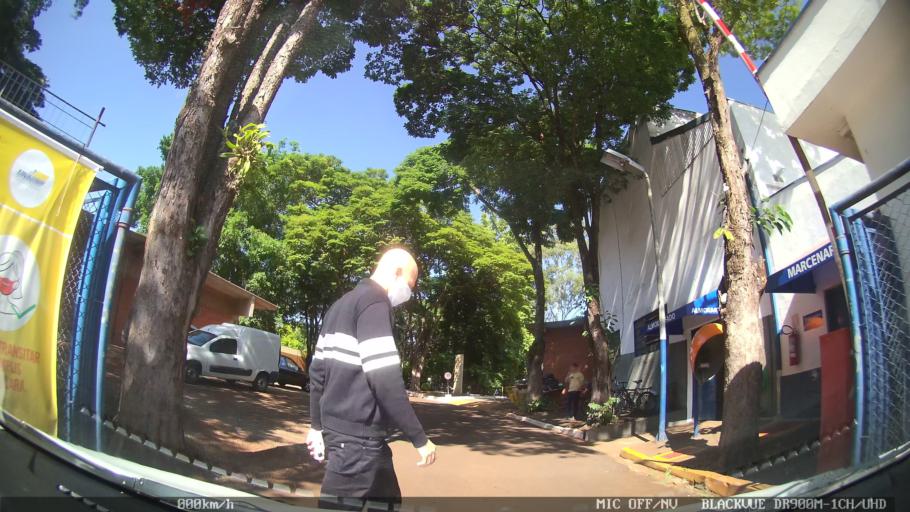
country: BR
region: Sao Paulo
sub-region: Ribeirao Preto
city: Ribeirao Preto
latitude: -21.1989
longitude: -47.7783
